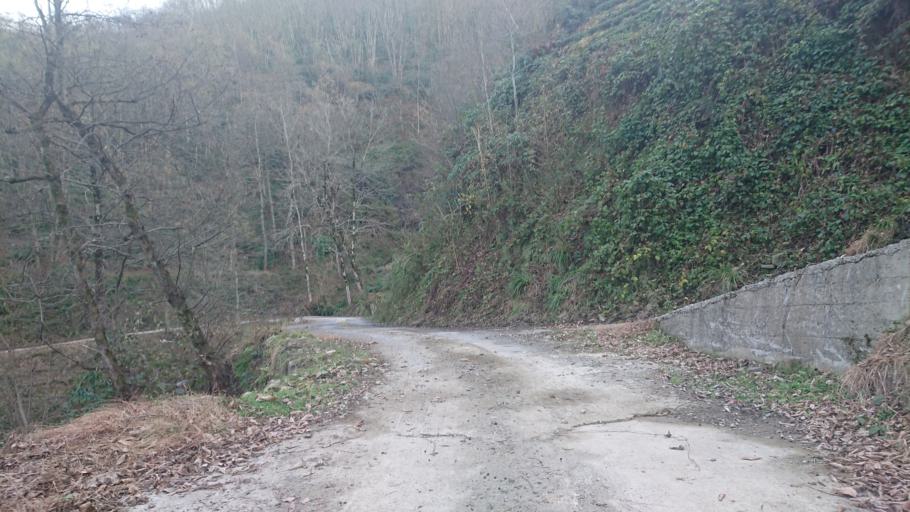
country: TR
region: Rize
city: Rize
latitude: 40.9770
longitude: 40.4947
